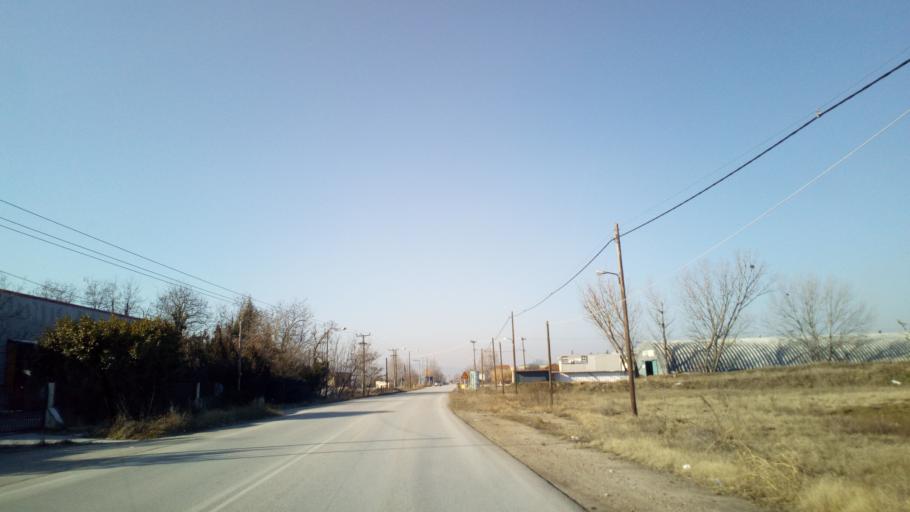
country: GR
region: Central Macedonia
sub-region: Nomos Thessalonikis
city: Kolchikon
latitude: 40.7500
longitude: 23.1032
